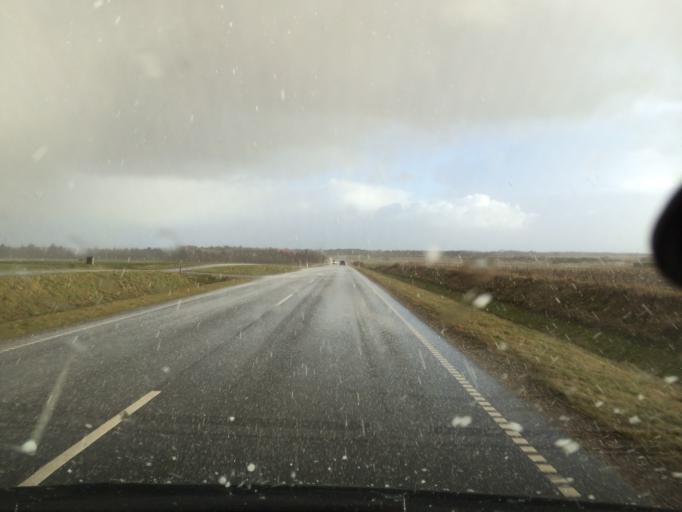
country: DK
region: Central Jutland
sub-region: Holstebro Kommune
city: Ulfborg
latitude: 56.2742
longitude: 8.2009
